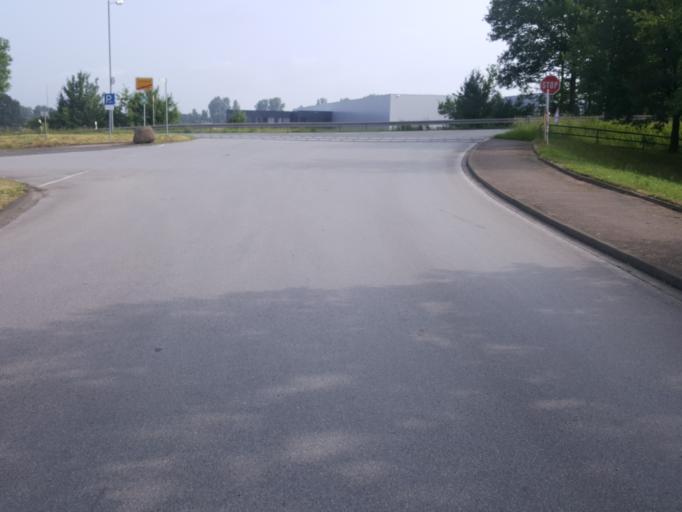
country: DE
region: North Rhine-Westphalia
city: Loehne
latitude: 52.1998
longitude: 8.7419
